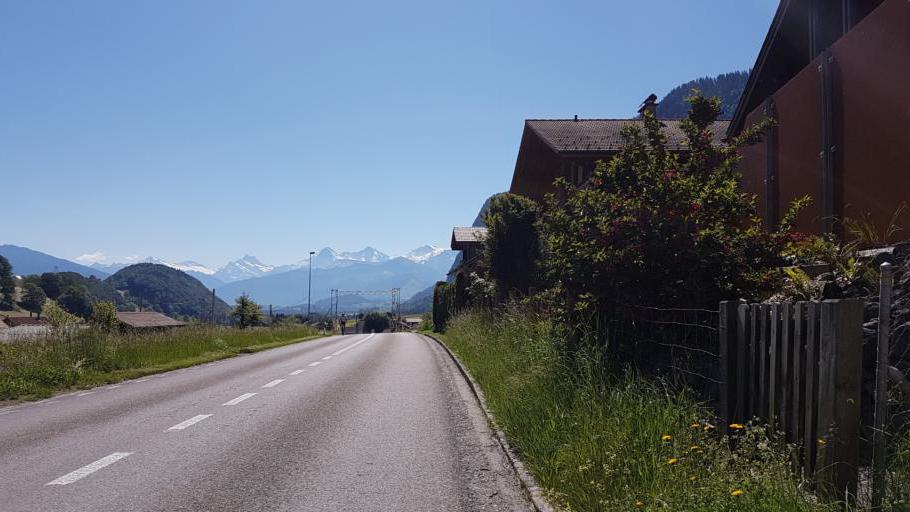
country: CH
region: Bern
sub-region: Thun District
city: Thierachern
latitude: 46.7172
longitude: 7.5545
